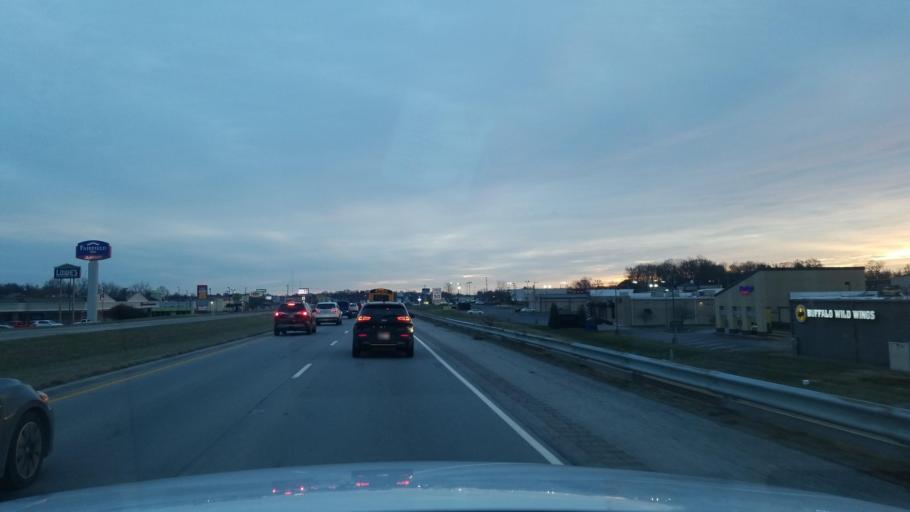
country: US
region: Indiana
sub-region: Vanderburgh County
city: Evansville
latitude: 37.9755
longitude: -87.6419
